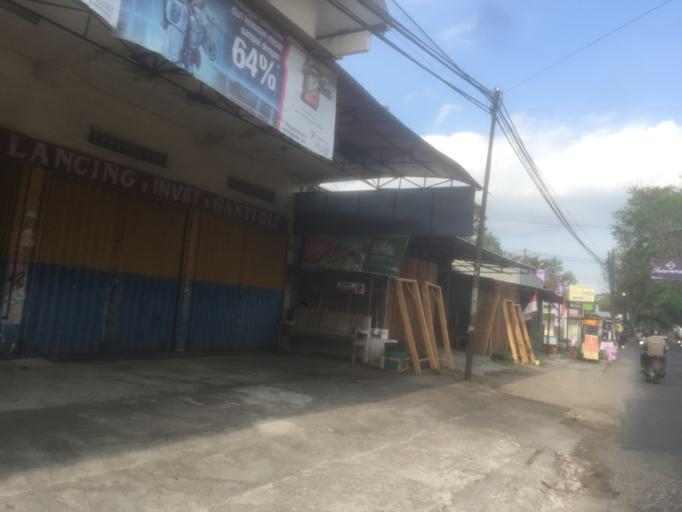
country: ID
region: Daerah Istimewa Yogyakarta
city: Melati
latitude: -7.7204
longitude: 110.3772
